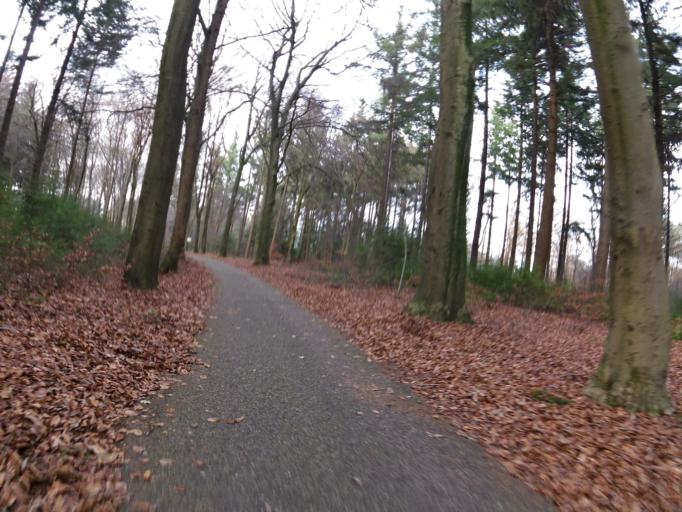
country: NL
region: North Brabant
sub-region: Gemeente Uden
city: Uden
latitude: 51.6889
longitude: 5.6275
